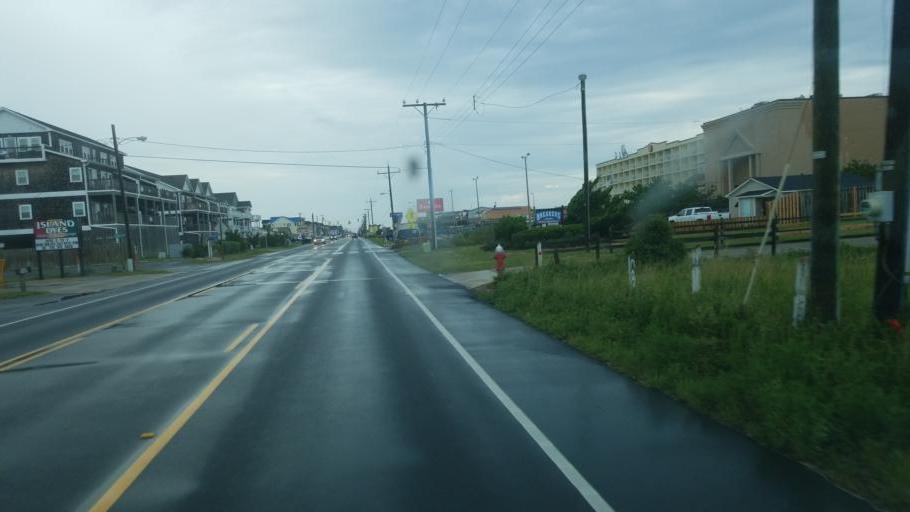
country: US
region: North Carolina
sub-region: Dare County
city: Kill Devil Hills
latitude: 35.9980
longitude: -75.6477
